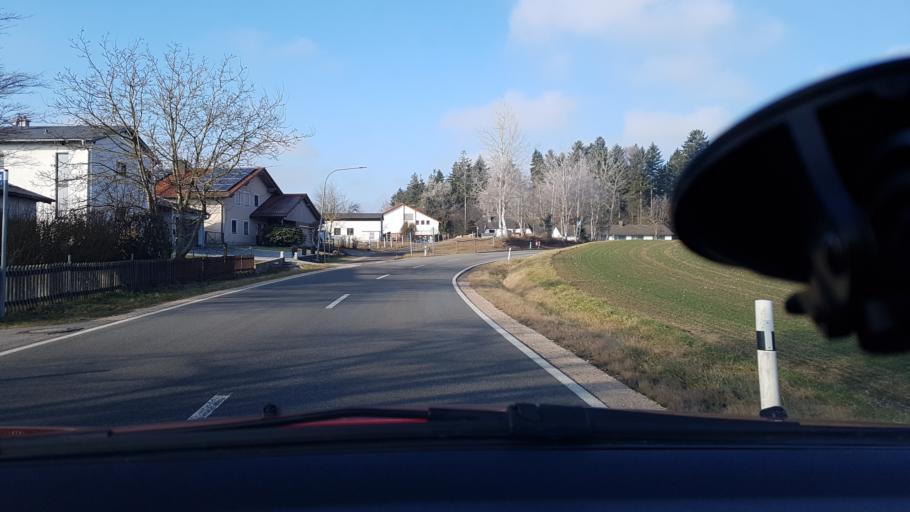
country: DE
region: Bavaria
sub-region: Lower Bavaria
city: Wittibreut
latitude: 48.3222
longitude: 12.9853
